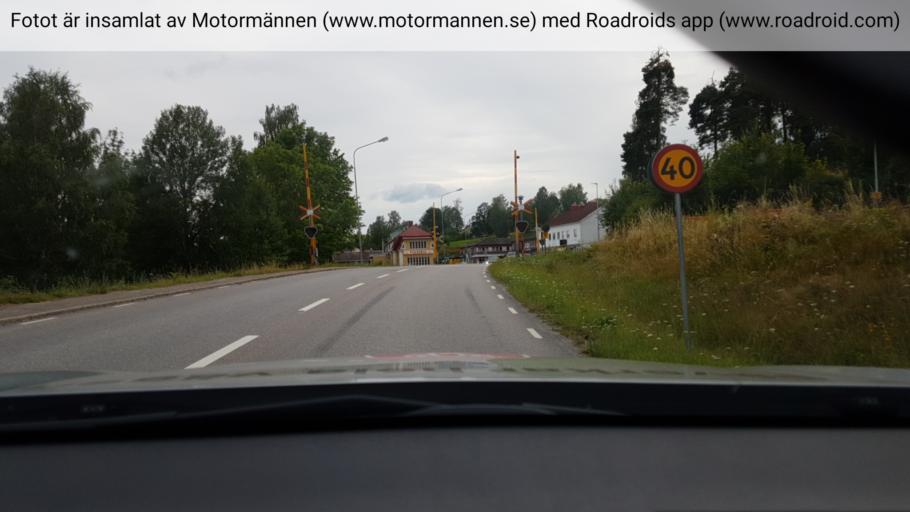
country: SE
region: Vaestra Goetaland
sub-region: Bengtsfors Kommun
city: Billingsfors
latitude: 58.9857
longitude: 12.2516
